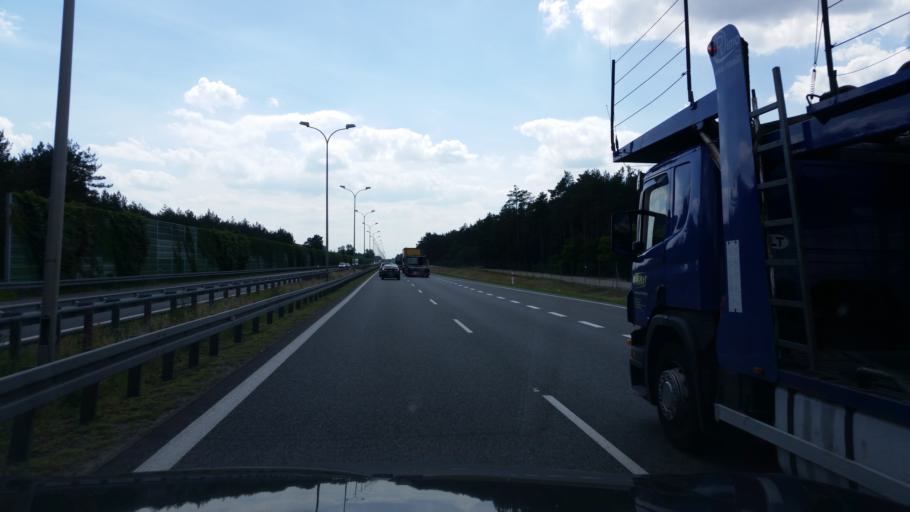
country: PL
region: Masovian Voivodeship
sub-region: Powiat wyszkowski
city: Wyszkow
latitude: 52.5304
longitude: 21.4236
